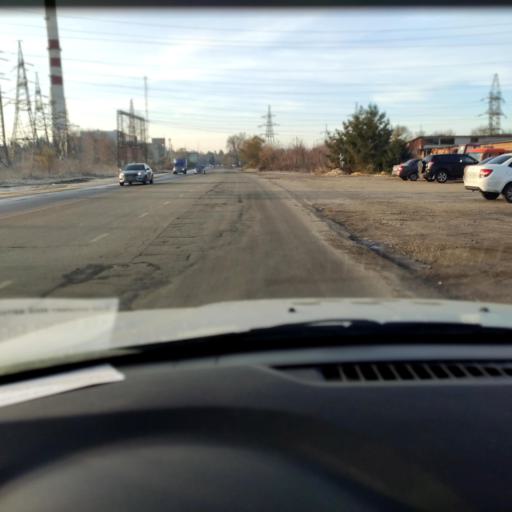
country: RU
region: Samara
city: Zhigulevsk
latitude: 53.5147
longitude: 49.4646
